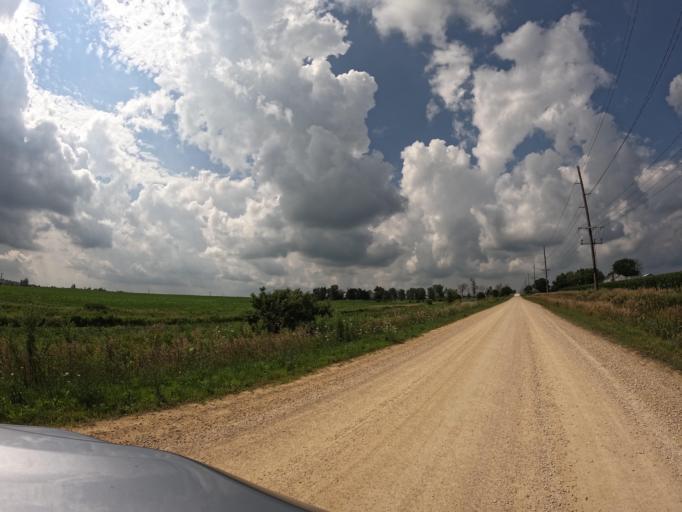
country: US
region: Iowa
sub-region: Clinton County
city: Camanche
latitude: 41.8020
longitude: -90.3159
